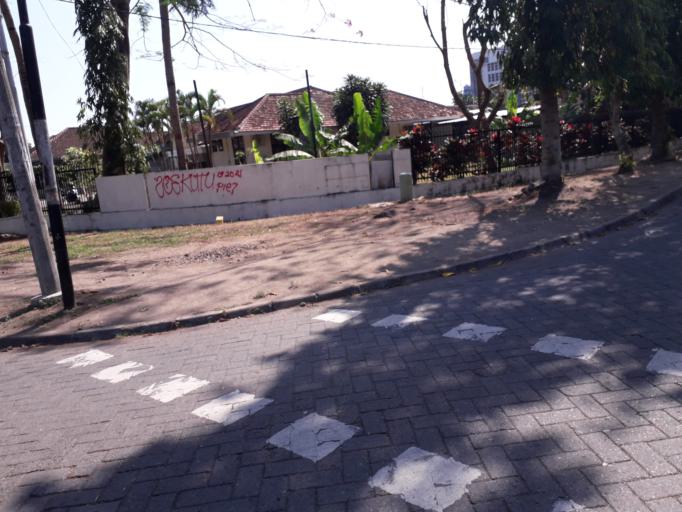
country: ID
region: Daerah Istimewa Yogyakarta
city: Yogyakarta
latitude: -7.7714
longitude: 110.3748
